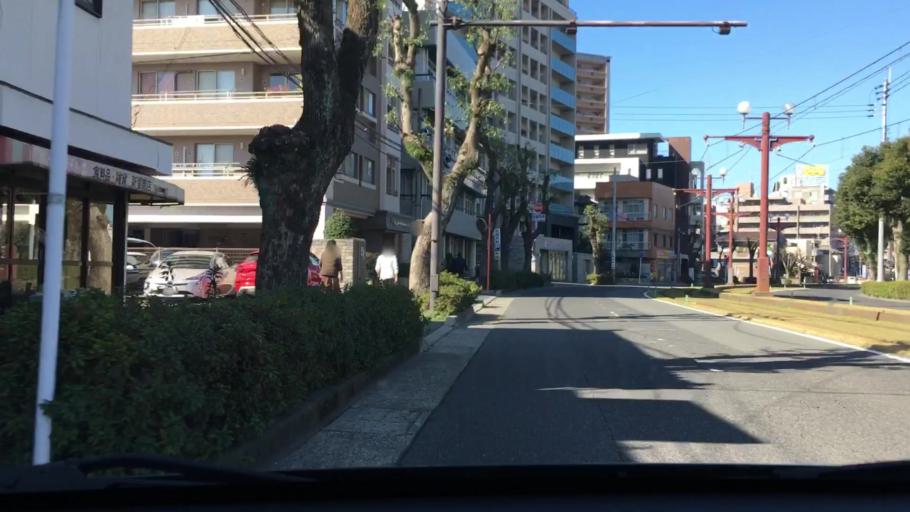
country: JP
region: Kagoshima
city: Kagoshima-shi
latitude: 31.5654
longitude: 130.5443
